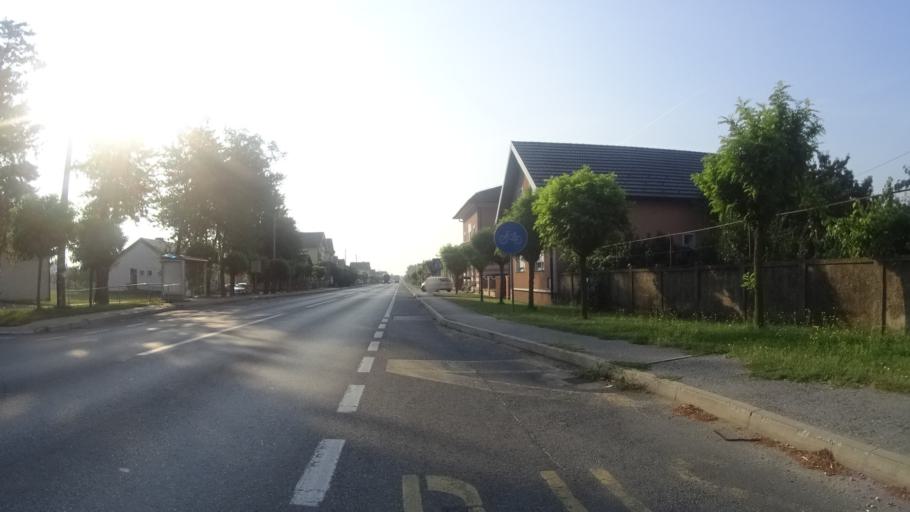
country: HR
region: Varazdinska
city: Sracinec
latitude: 46.3282
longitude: 16.2829
